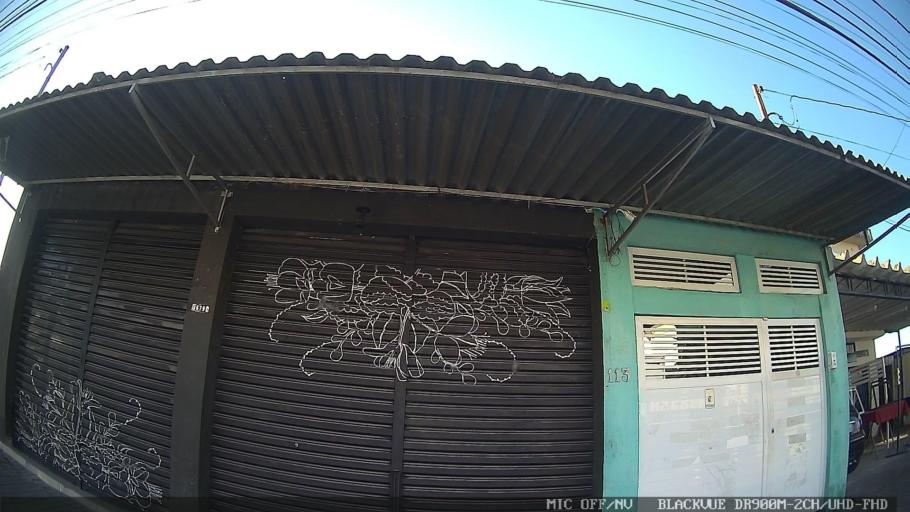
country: BR
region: Sao Paulo
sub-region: Santos
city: Santos
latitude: -23.9626
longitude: -46.2952
